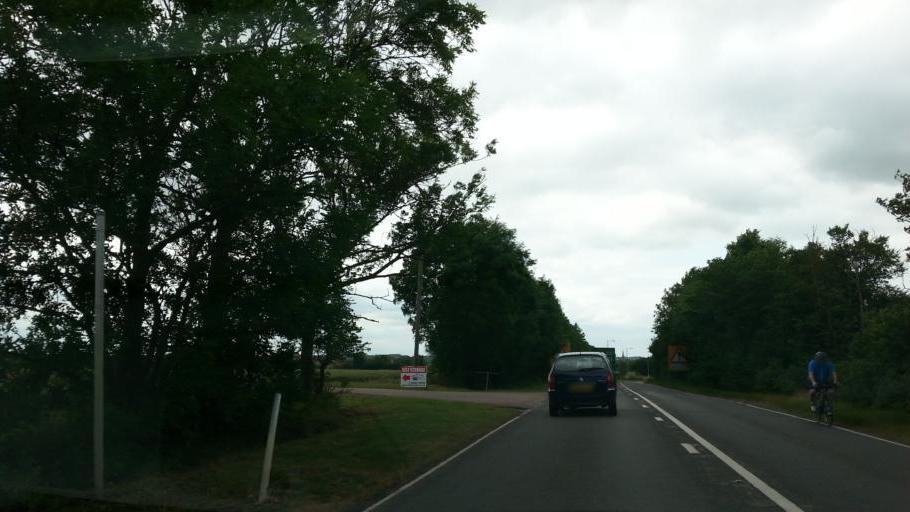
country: GB
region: England
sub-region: Cambridgeshire
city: Godmanchester
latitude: 52.3066
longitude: -0.1619
